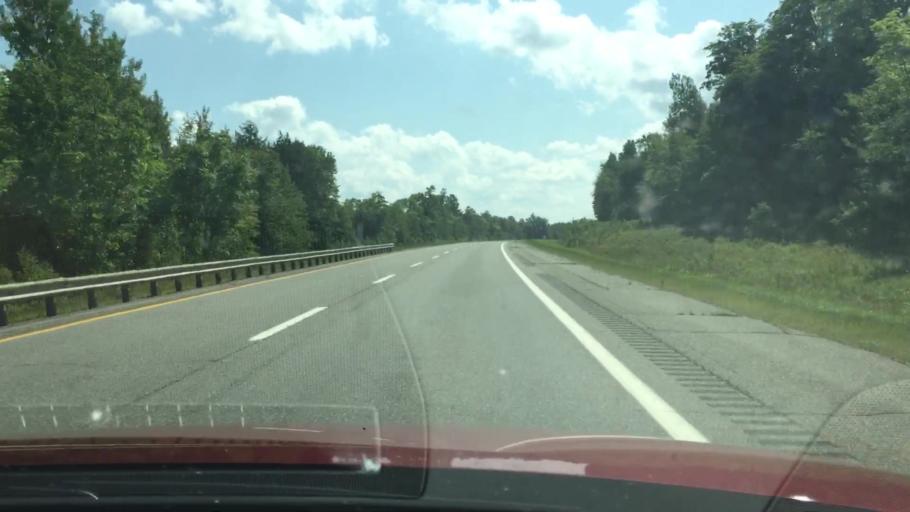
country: US
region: Maine
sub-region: Penobscot County
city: Lincoln
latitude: 45.4320
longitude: -68.5895
